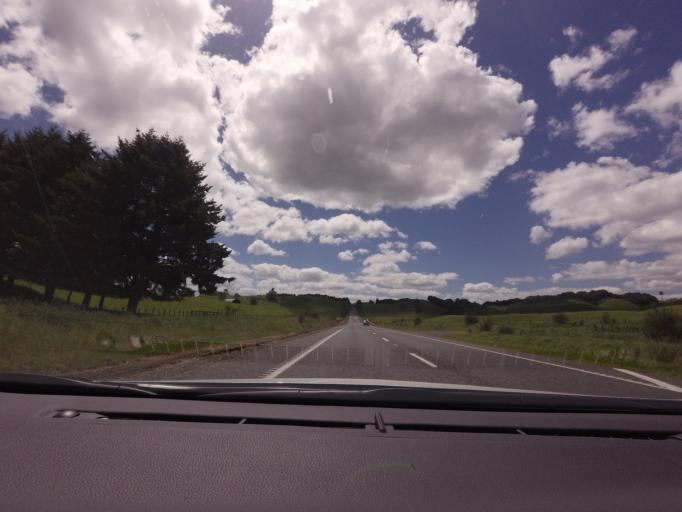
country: NZ
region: Bay of Plenty
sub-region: Rotorua District
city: Rotorua
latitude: -38.2588
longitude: 176.3197
